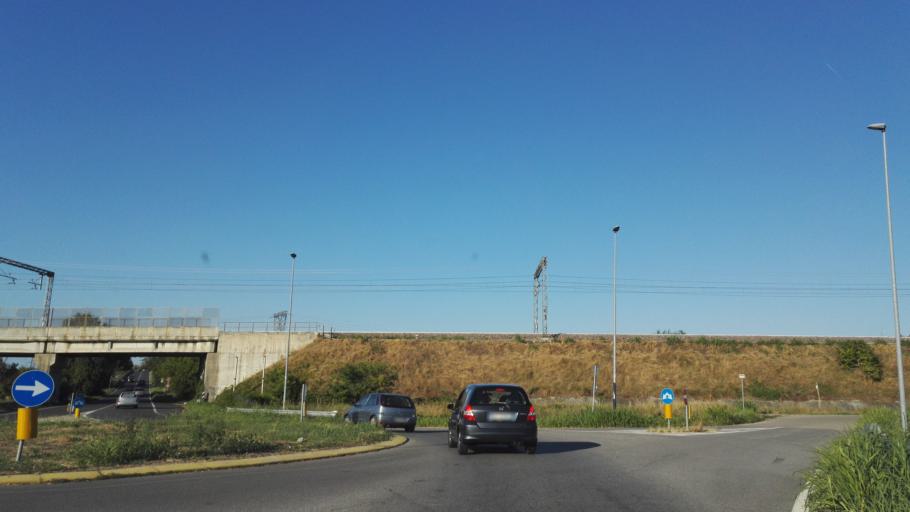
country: IT
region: Lombardy
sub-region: Citta metropolitana di Milano
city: San Giuliano Milanese
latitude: 45.3852
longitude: 9.2860
